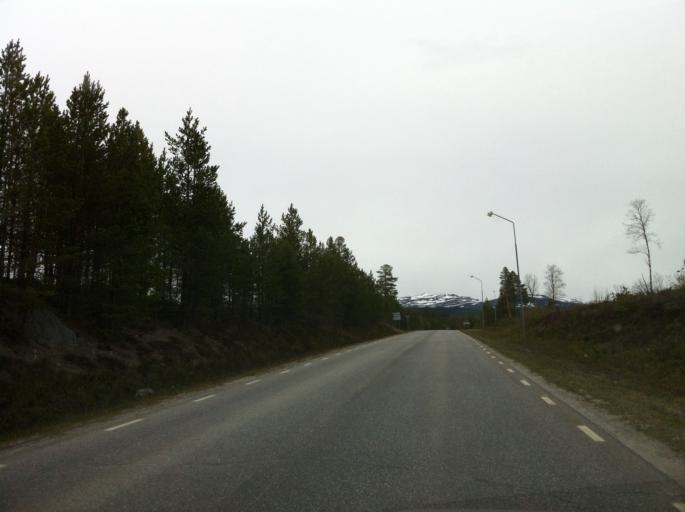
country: NO
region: Hedmark
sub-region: Engerdal
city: Engerdal
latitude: 62.5281
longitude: 12.5753
